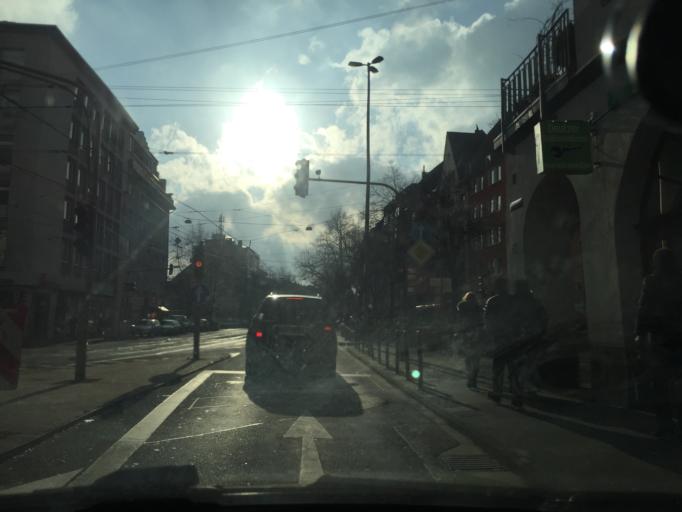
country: DE
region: North Rhine-Westphalia
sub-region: Regierungsbezirk Koln
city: Deutz
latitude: 50.9374
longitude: 6.9780
